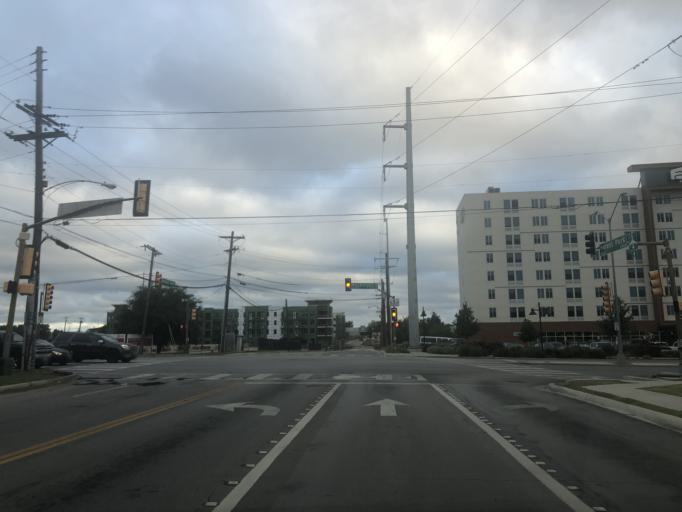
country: US
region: Texas
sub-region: Dallas County
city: University Park
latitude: 32.8254
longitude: -96.8472
